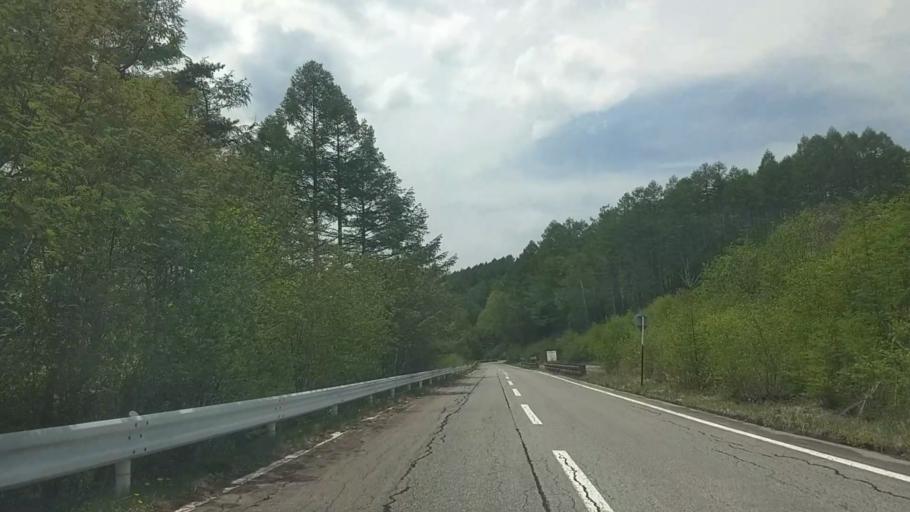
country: JP
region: Nagano
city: Saku
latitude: 36.0910
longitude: 138.3911
